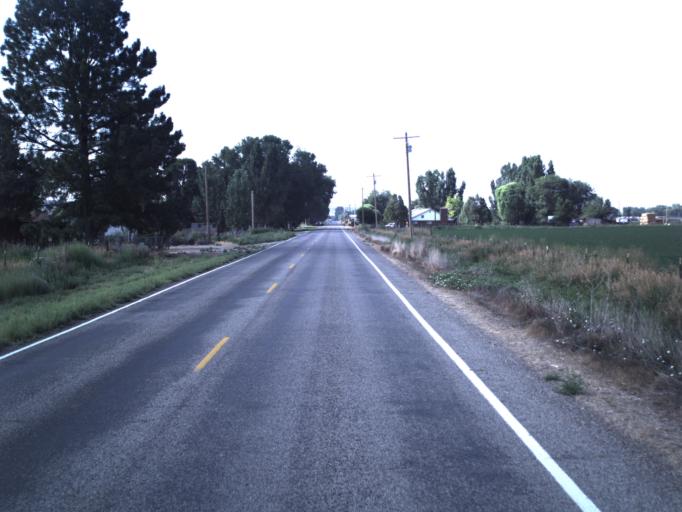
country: US
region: Utah
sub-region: Uintah County
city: Naples
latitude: 40.3802
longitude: -109.3458
